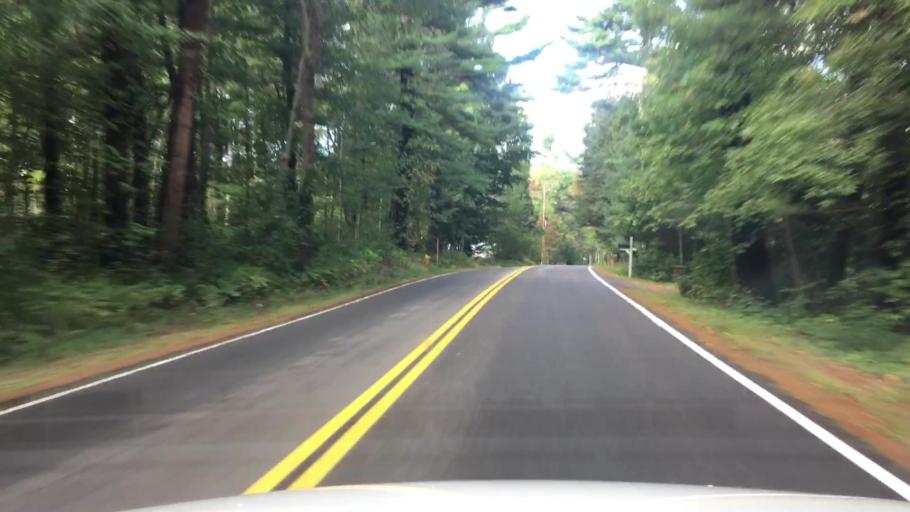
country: US
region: Maine
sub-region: York County
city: Kittery Point
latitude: 43.0897
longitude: -70.7048
